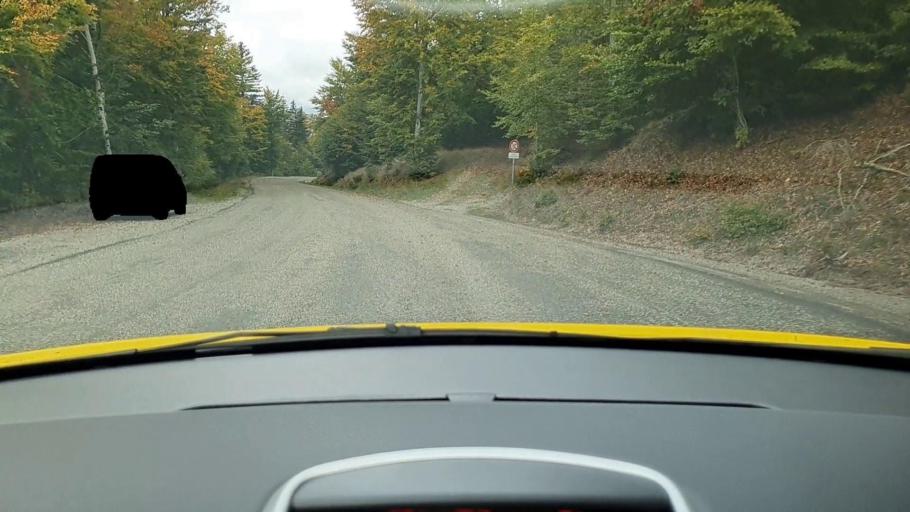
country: FR
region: Languedoc-Roussillon
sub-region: Departement du Gard
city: Le Vigan
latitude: 44.0586
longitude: 3.5466
